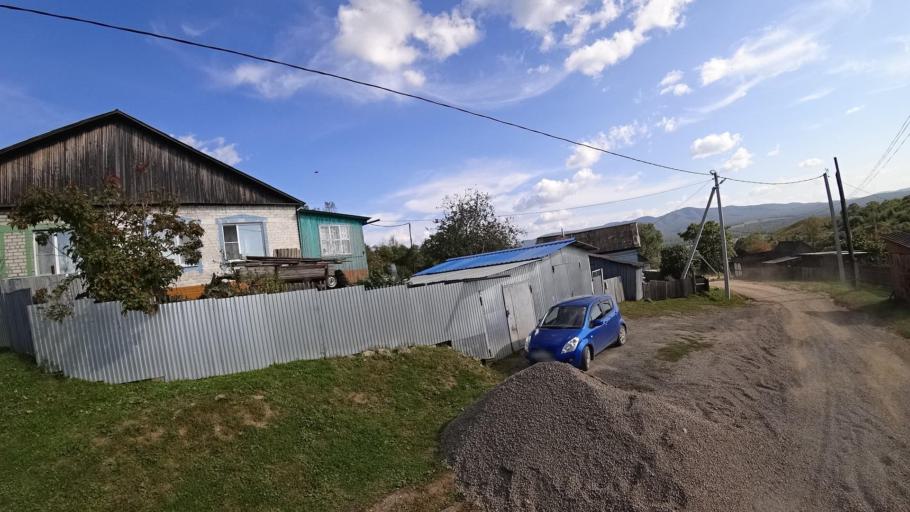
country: RU
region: Jewish Autonomous Oblast
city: Birakan
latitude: 48.9982
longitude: 131.7121
